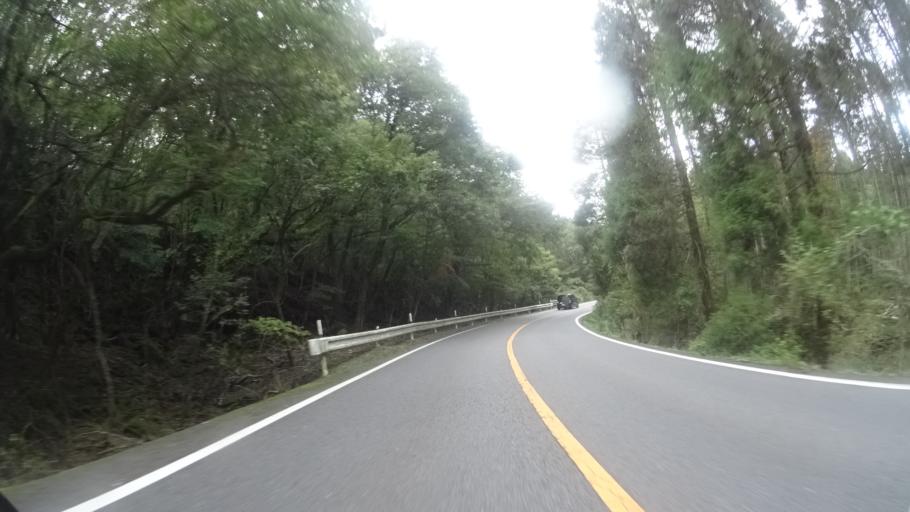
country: JP
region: Oita
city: Beppu
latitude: 33.2698
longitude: 131.4079
